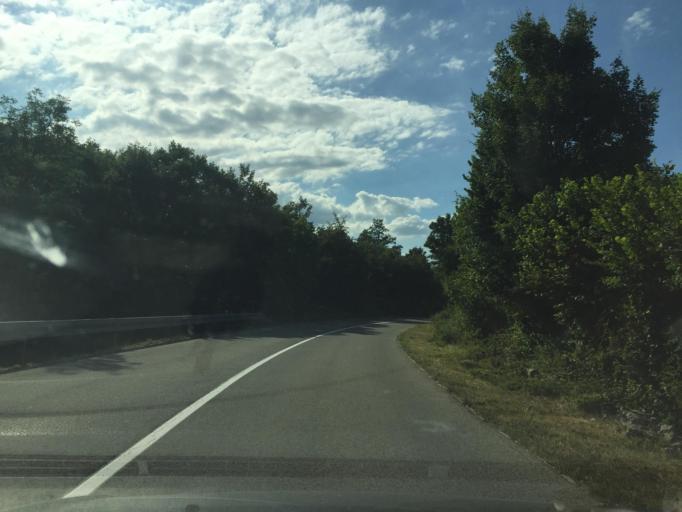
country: HR
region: Primorsko-Goranska
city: Klana
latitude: 45.4518
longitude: 14.3196
